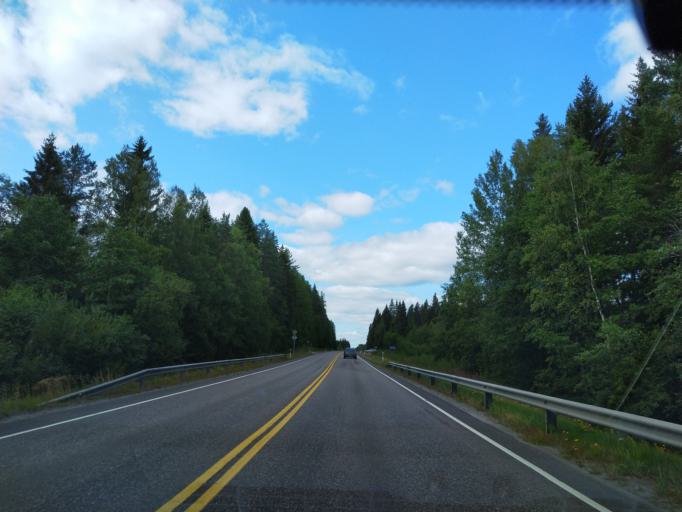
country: FI
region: Haeme
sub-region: Haemeenlinna
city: Renko
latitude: 60.7611
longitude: 24.2854
